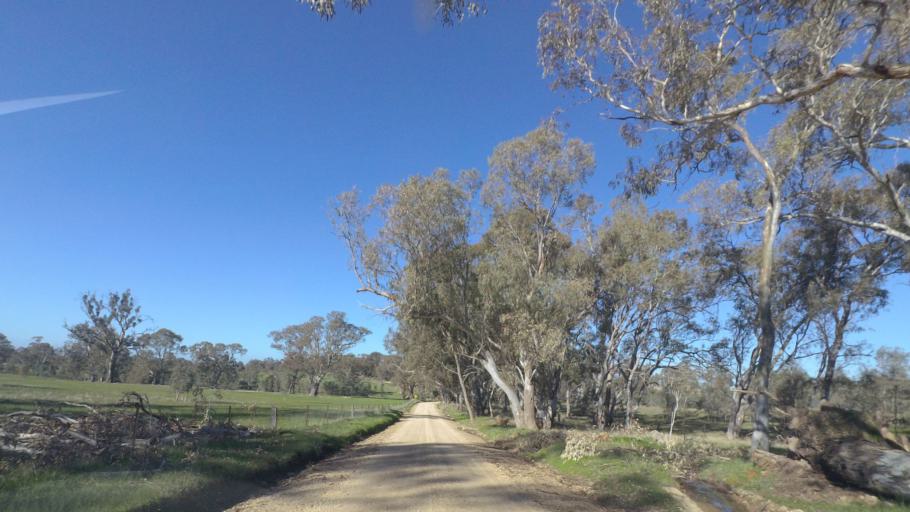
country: AU
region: Victoria
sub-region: Mount Alexander
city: Castlemaine
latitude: -36.9661
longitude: 144.3447
